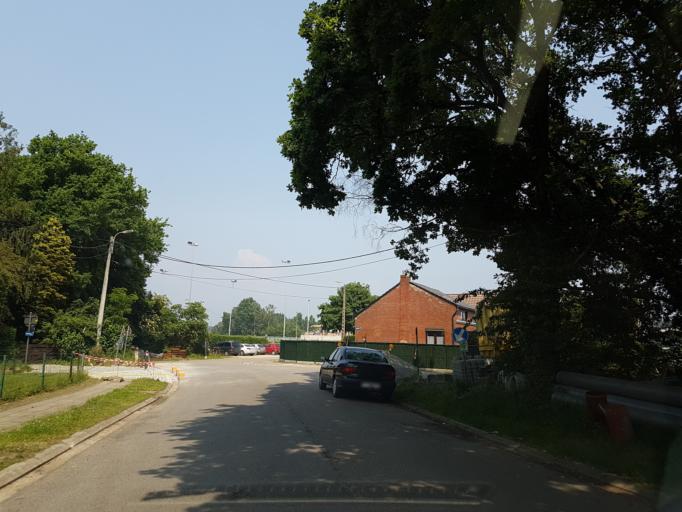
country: BE
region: Flanders
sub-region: Provincie Vlaams-Brabant
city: Zemst
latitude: 50.9681
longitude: 4.5002
